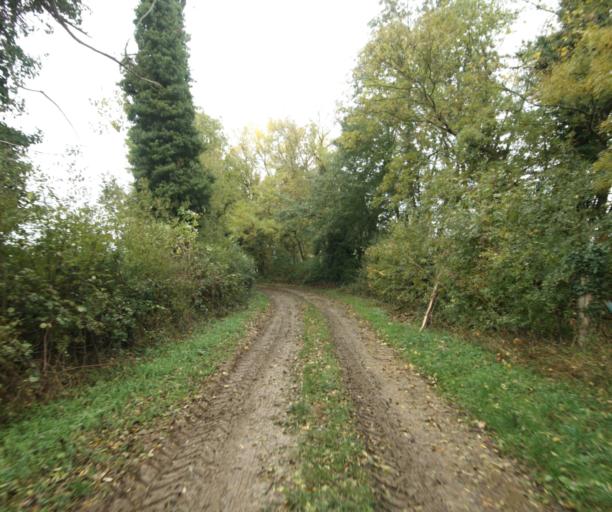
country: FR
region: Rhone-Alpes
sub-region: Departement de l'Ain
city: Pont-de-Vaux
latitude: 46.4771
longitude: 4.9036
